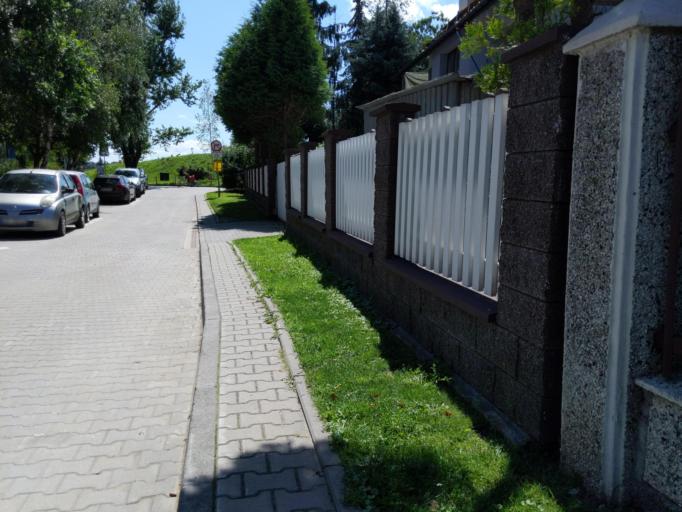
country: PL
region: Lesser Poland Voivodeship
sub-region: Krakow
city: Krakow
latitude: 50.0353
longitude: 19.9933
